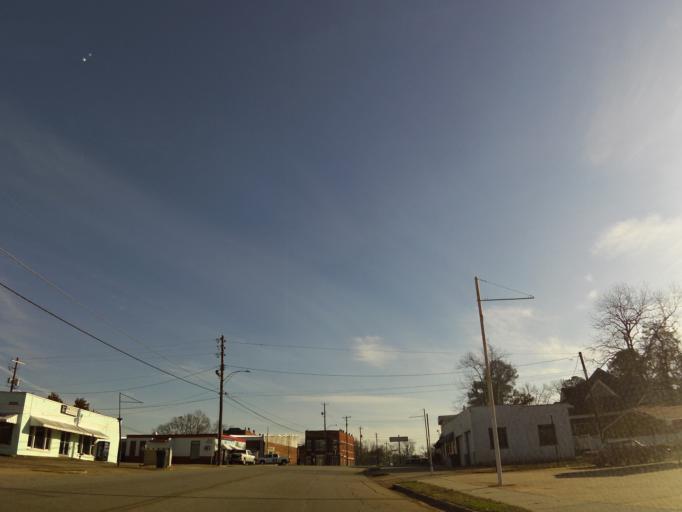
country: US
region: Georgia
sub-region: Stewart County
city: Richland
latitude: 32.0909
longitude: -84.6675
